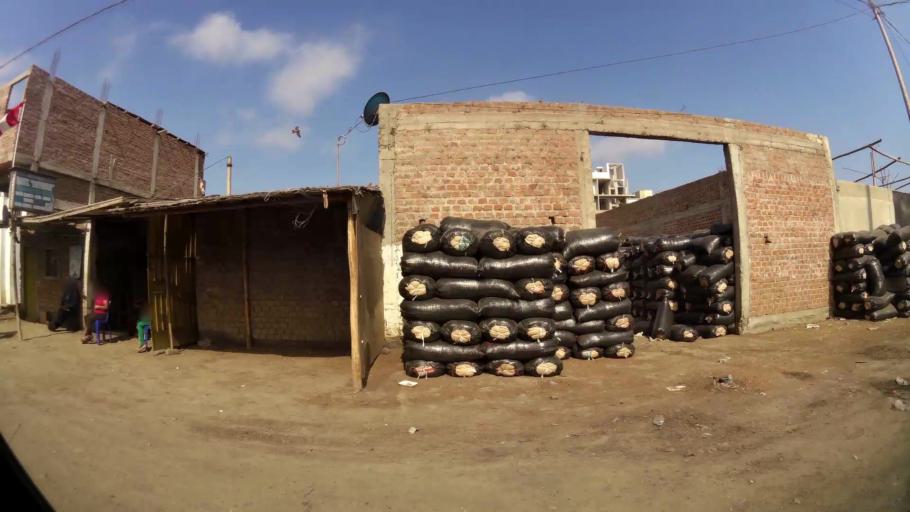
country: PE
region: La Libertad
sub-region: Provincia de Trujillo
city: Trujillo
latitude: -8.1186
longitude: -79.0146
